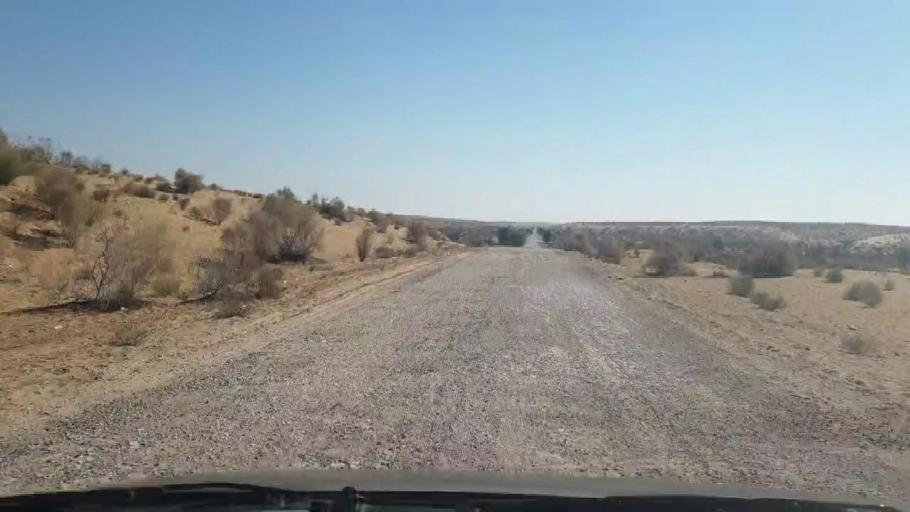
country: PK
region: Sindh
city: Bozdar
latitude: 27.0432
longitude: 68.6856
